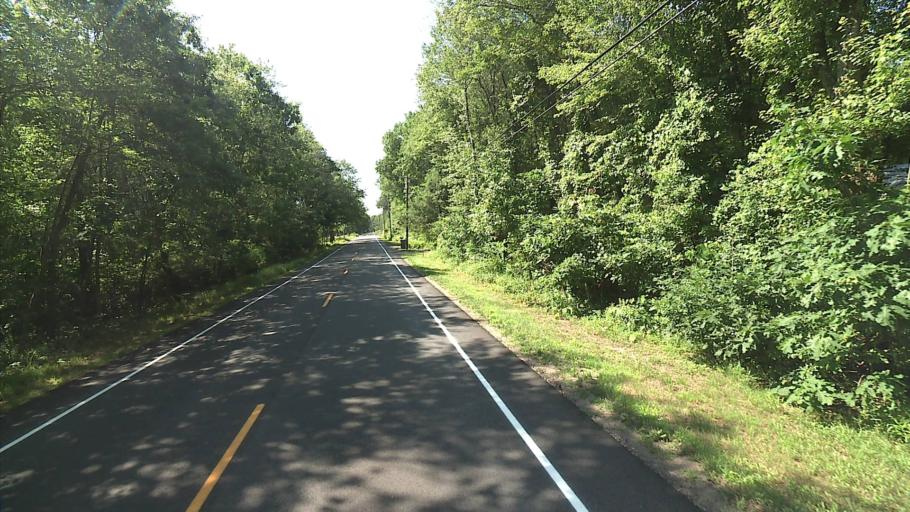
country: US
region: Connecticut
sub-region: Litchfield County
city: Northwest Harwinton
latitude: 41.7552
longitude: -73.0239
